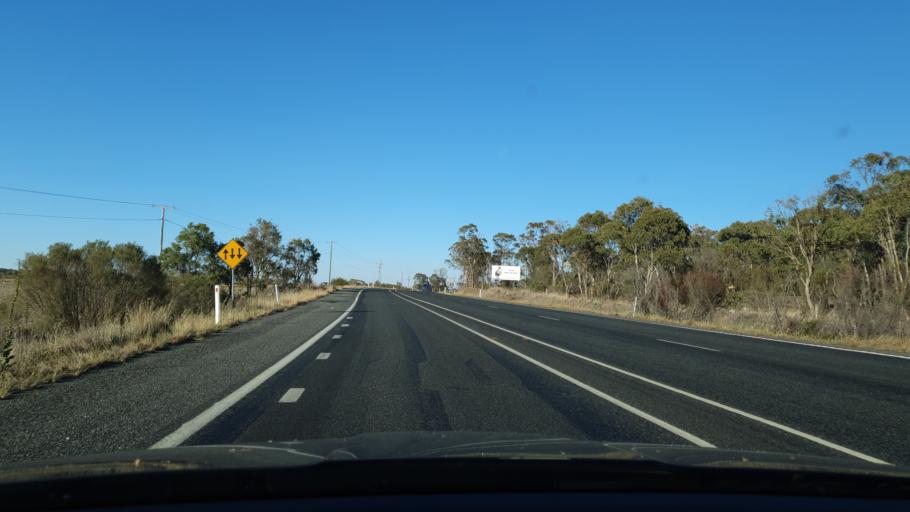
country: AU
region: Queensland
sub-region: Southern Downs
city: Stanthorpe
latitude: -28.6879
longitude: 151.9114
